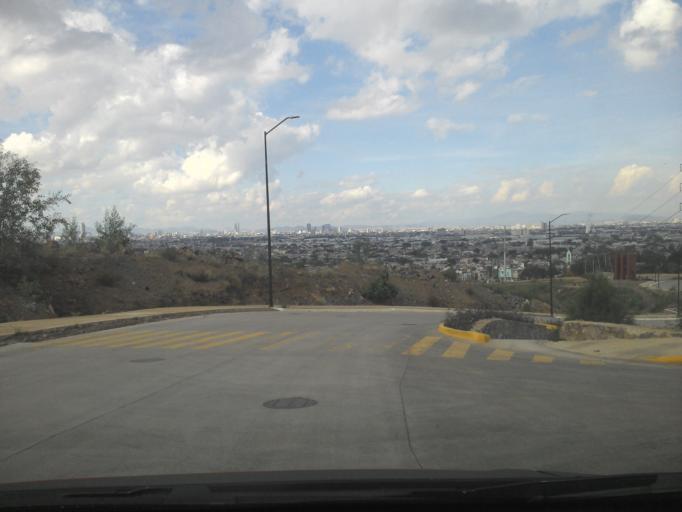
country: MX
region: Jalisco
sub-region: Tlajomulco de Zuniga
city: Altus Bosques
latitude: 20.6120
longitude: -103.3636
